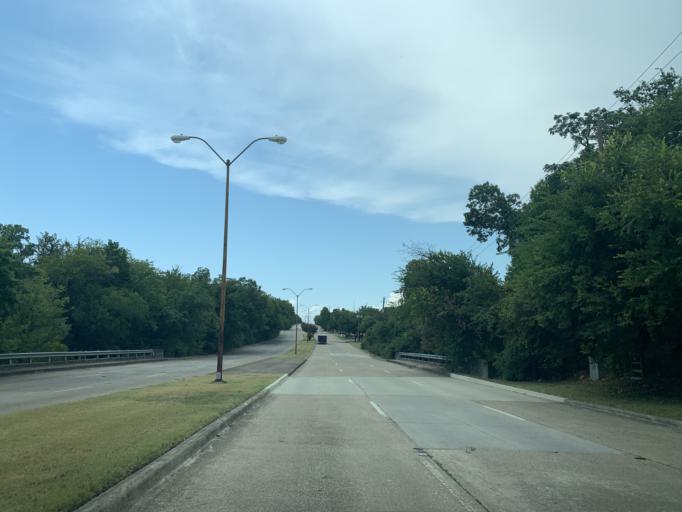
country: US
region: Texas
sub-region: Dallas County
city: Lancaster
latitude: 32.6648
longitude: -96.8057
